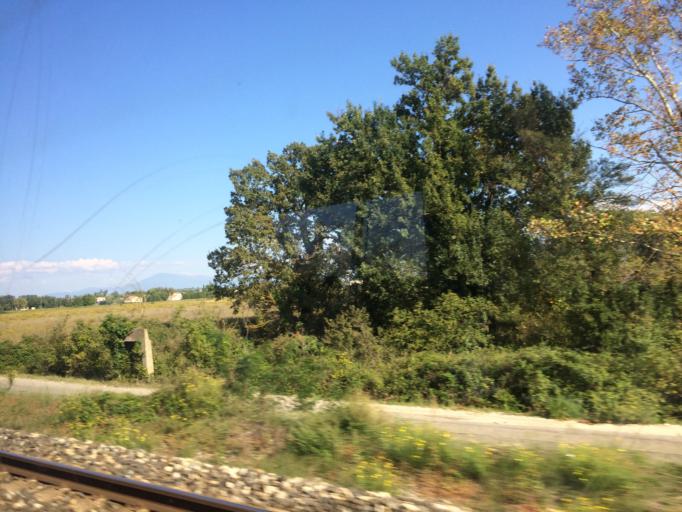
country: FR
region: Provence-Alpes-Cote d'Azur
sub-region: Departement du Vaucluse
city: Le Pontet
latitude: 43.9816
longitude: 4.8651
